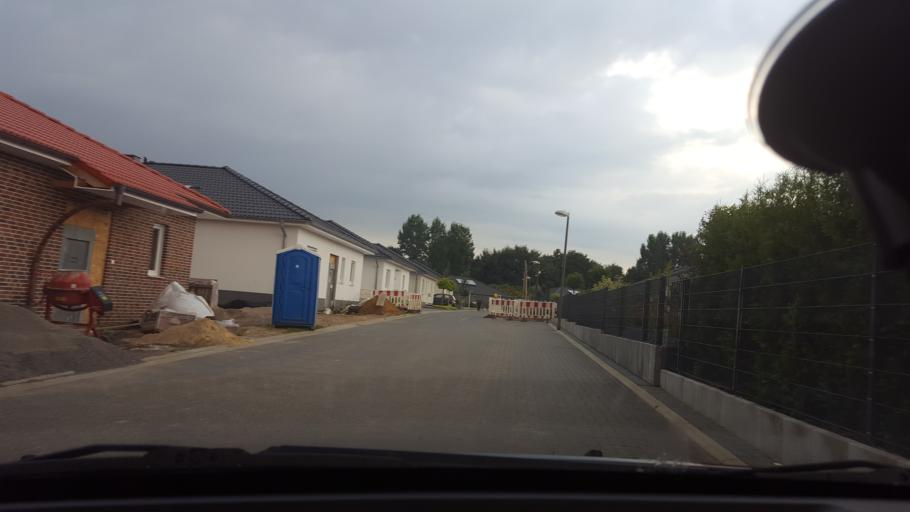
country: DE
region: North Rhine-Westphalia
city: Marl
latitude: 51.6538
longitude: 7.1407
